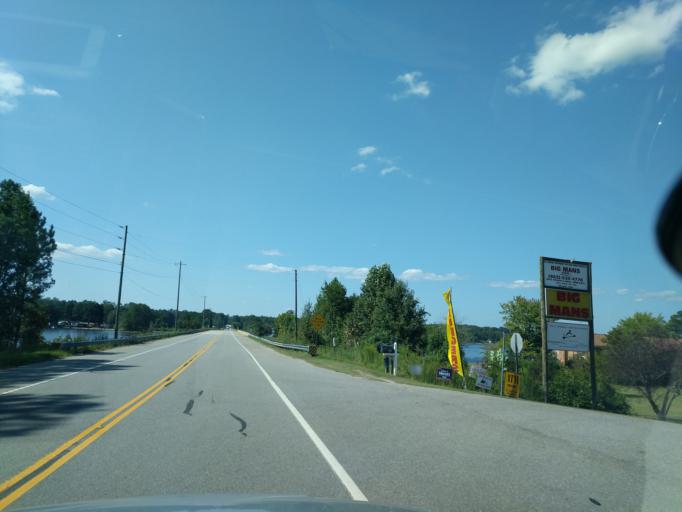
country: US
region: South Carolina
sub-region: Newberry County
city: Prosperity
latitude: 34.0781
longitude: -81.5607
